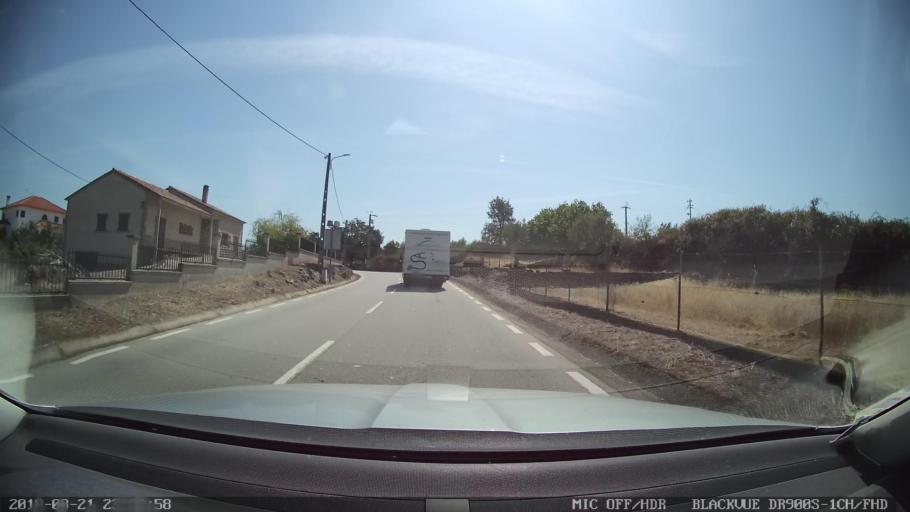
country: PT
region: Guarda
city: Alcains
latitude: 39.8790
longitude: -7.3934
